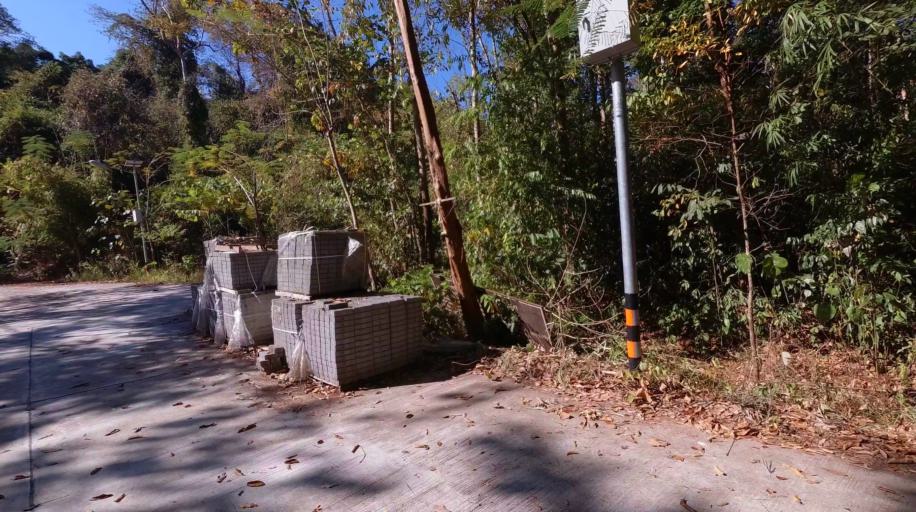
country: TH
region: Trat
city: Ko Kut
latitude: 11.6285
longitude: 102.5579
